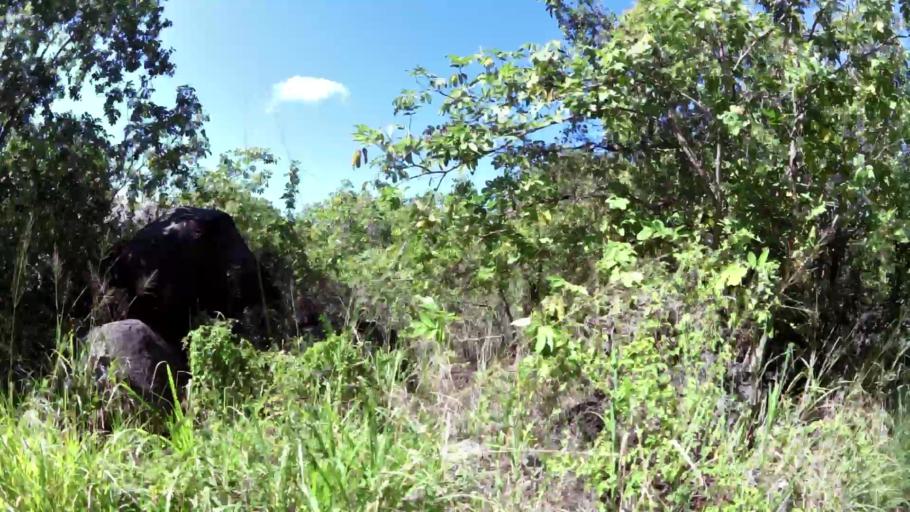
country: VG
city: Tortola
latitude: 18.4438
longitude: -64.5326
